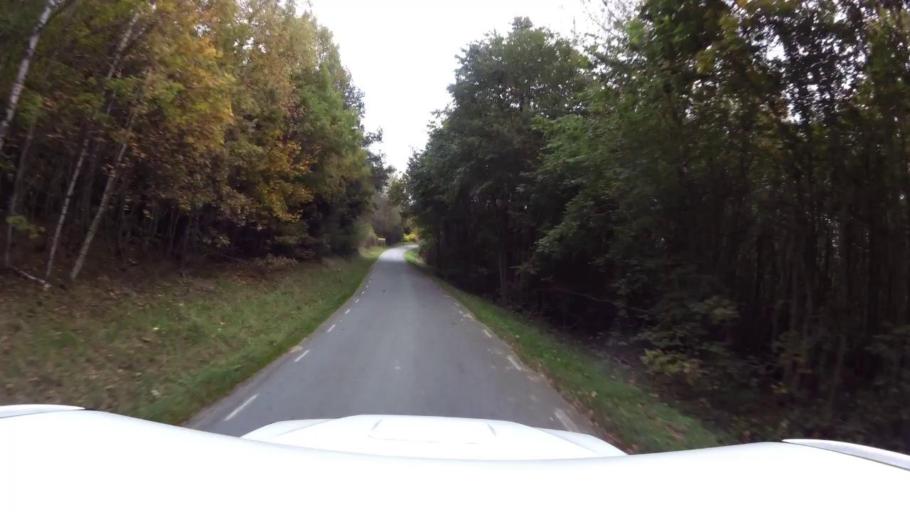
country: SE
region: OEstergoetland
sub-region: Linkopings Kommun
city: Ljungsbro
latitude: 58.5252
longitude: 15.4724
